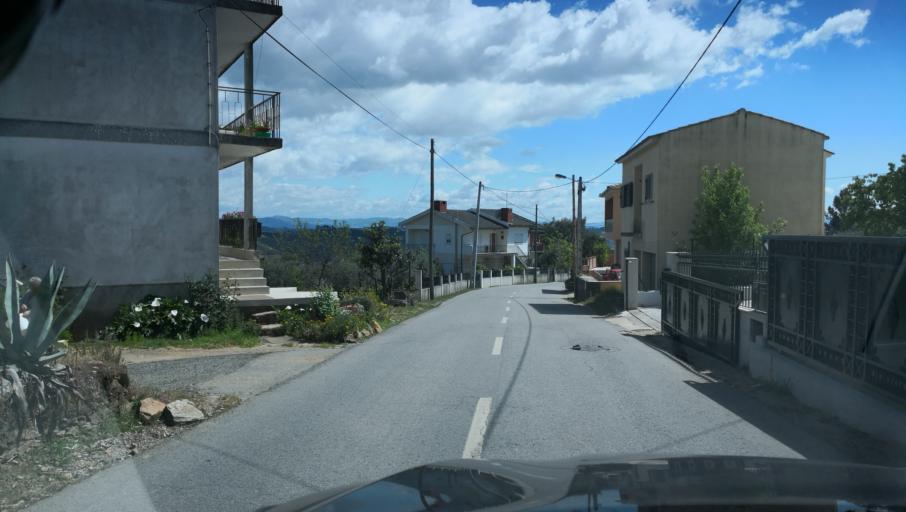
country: PT
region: Vila Real
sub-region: Vila Real
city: Vila Real
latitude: 41.2632
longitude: -7.7305
